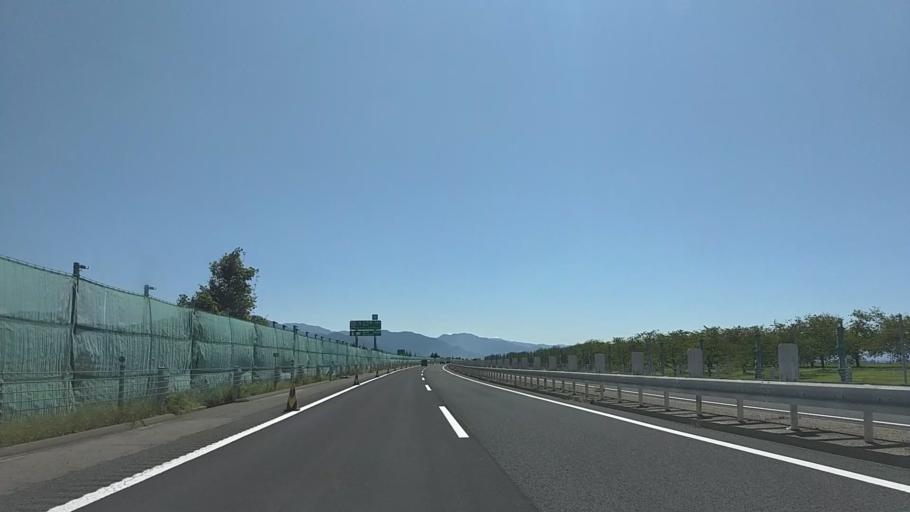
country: JP
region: Nagano
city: Nakano
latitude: 36.7191
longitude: 138.3134
